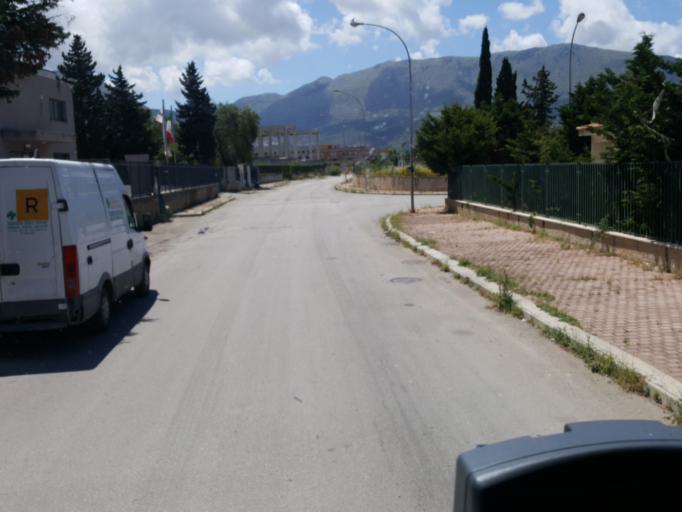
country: IT
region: Sicily
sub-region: Palermo
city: Carini
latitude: 38.1535
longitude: 13.2093
